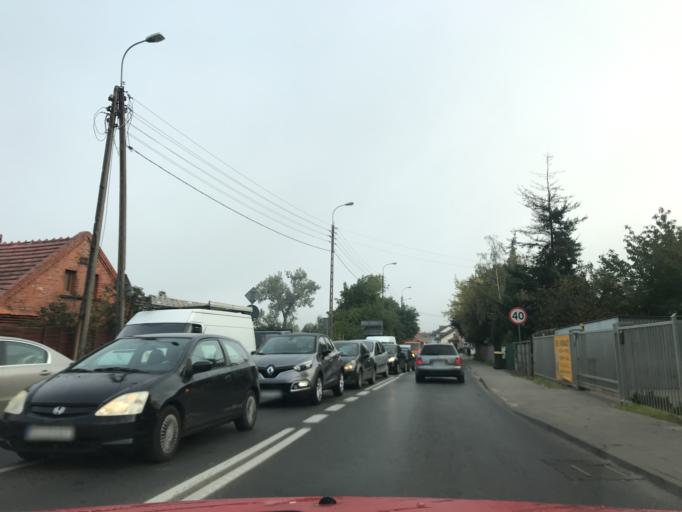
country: PL
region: Greater Poland Voivodeship
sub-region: Powiat poznanski
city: Baranowo
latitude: 52.4325
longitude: 16.8086
